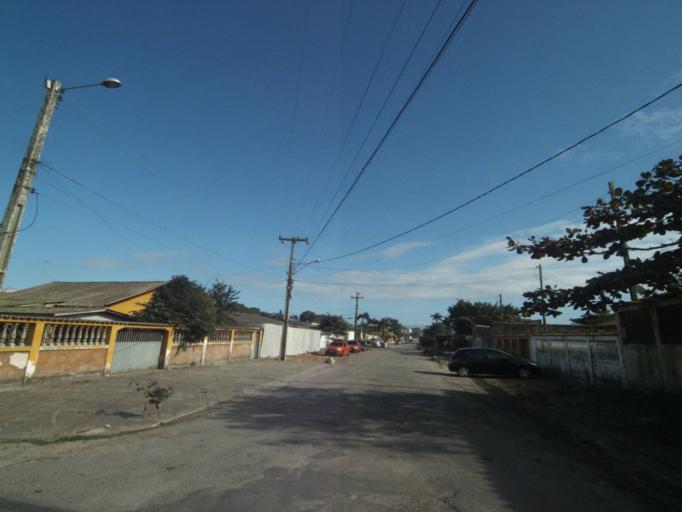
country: BR
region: Parana
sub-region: Paranagua
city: Paranagua
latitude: -25.5107
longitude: -48.5260
